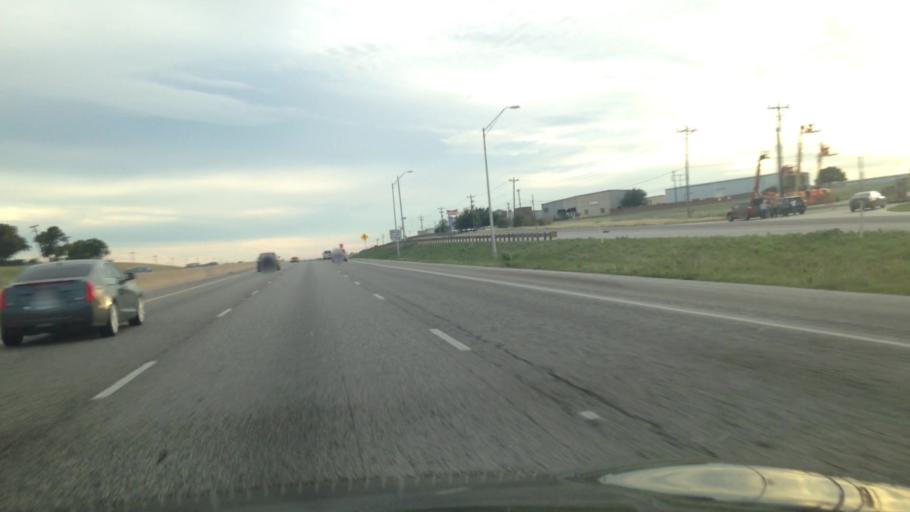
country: US
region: Texas
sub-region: Hays County
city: Buda
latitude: 30.0698
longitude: -97.8286
